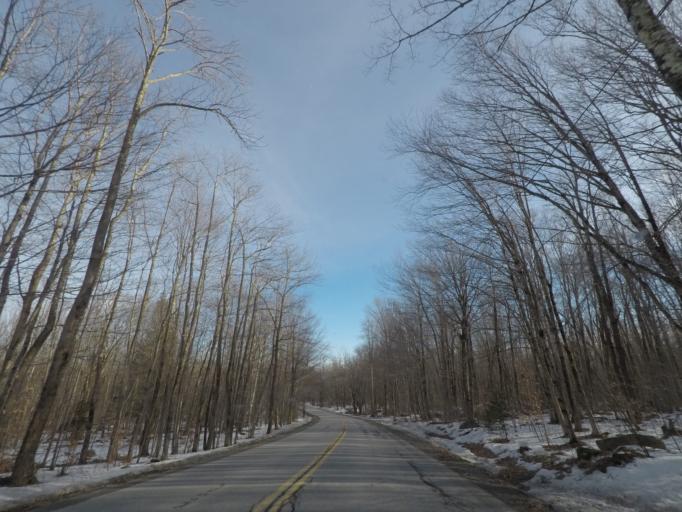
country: US
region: New York
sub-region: Rensselaer County
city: Poestenkill
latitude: 42.7458
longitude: -73.4122
